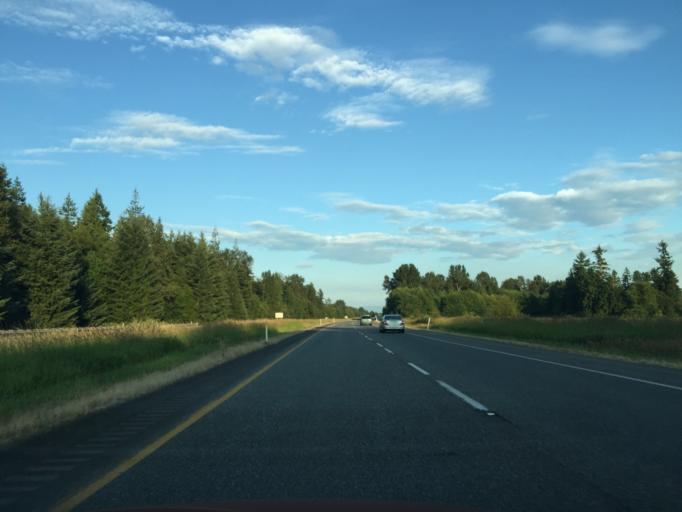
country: US
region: Washington
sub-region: Whatcom County
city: Blaine
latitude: 48.9618
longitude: -122.7031
